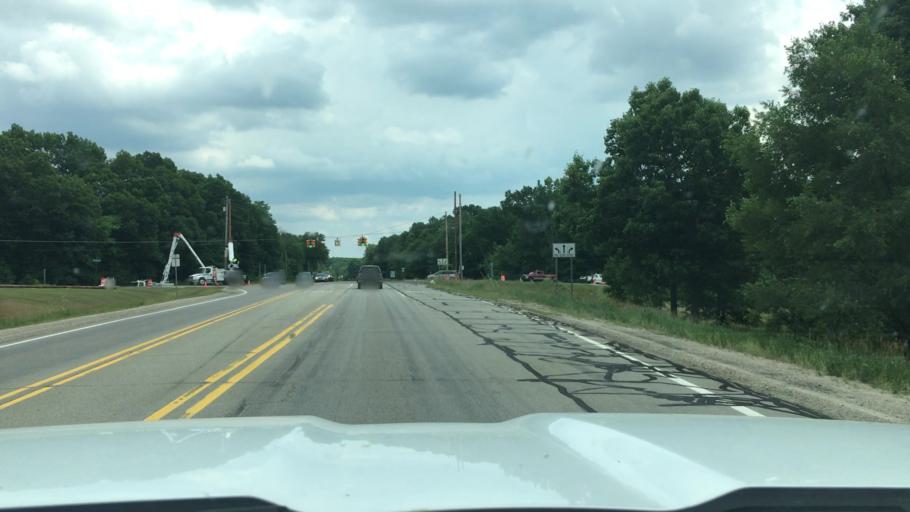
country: US
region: Michigan
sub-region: Montcalm County
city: Greenville
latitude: 43.1752
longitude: -85.3541
